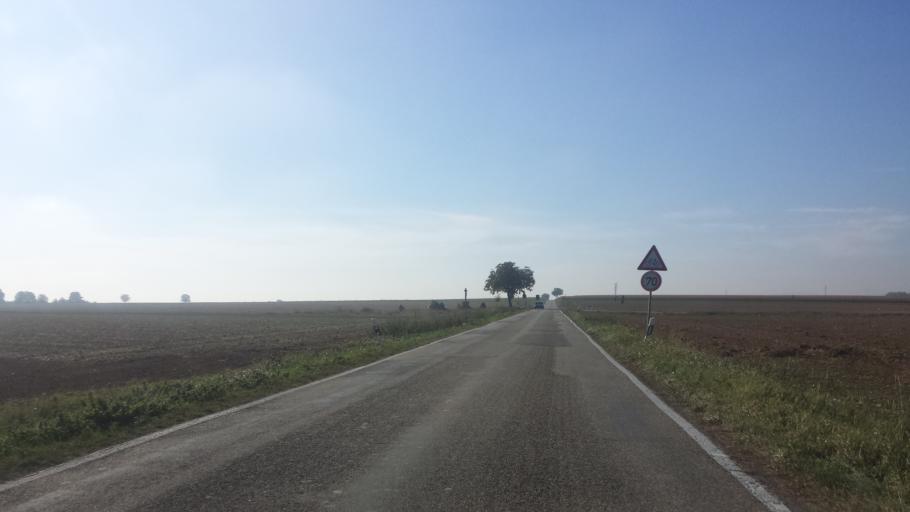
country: DE
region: Rheinland-Pfalz
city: Offenbach an der Queich
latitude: 49.1743
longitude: 8.1725
